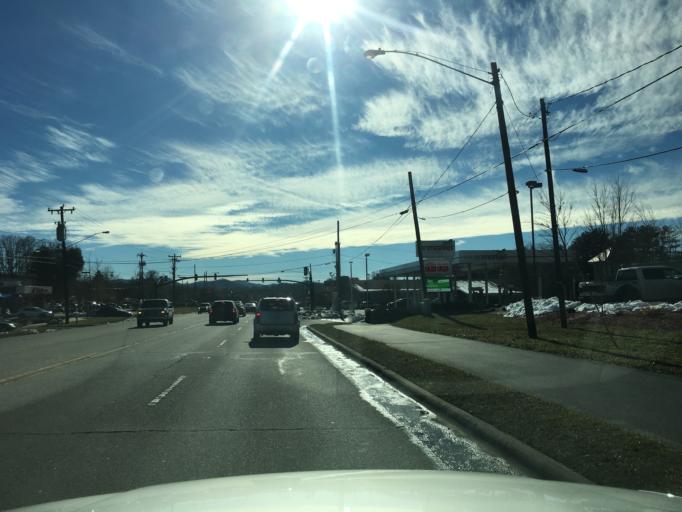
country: US
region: North Carolina
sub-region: Transylvania County
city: Brevard
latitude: 35.2494
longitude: -82.7219
